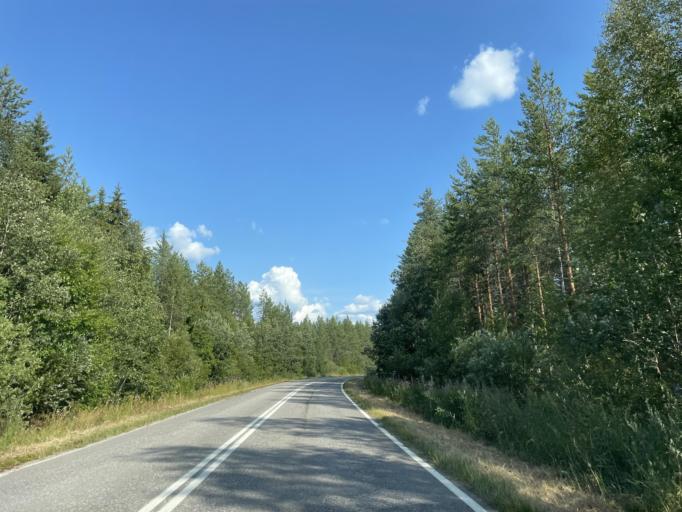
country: FI
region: Central Finland
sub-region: Saarijaervi-Viitasaari
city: Pihtipudas
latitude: 63.3659
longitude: 25.7087
